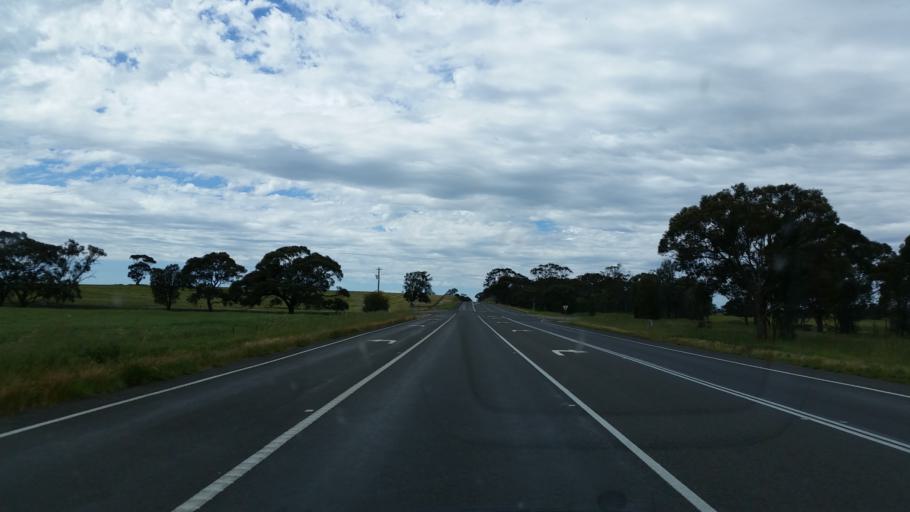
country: AU
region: South Australia
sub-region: Tatiara
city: Bordertown
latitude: -36.3466
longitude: 140.9829
